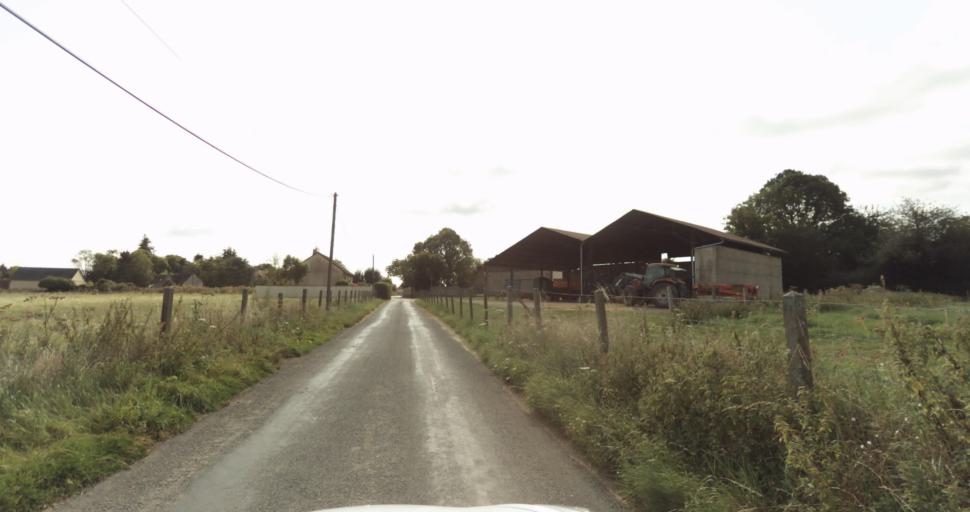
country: FR
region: Haute-Normandie
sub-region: Departement de l'Eure
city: Tillieres-sur-Avre
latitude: 48.7573
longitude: 1.1051
